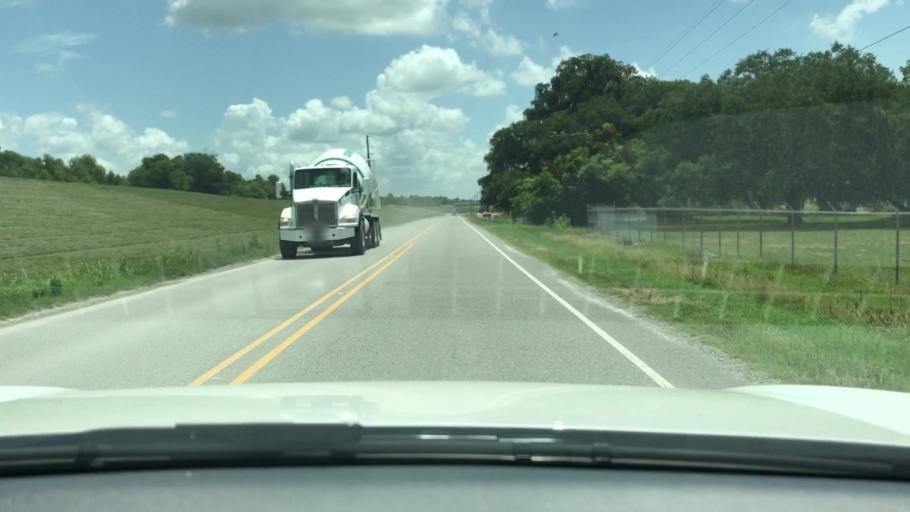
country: US
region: Louisiana
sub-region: Iberville Parish
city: Plaquemine
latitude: 30.2732
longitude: -91.1797
